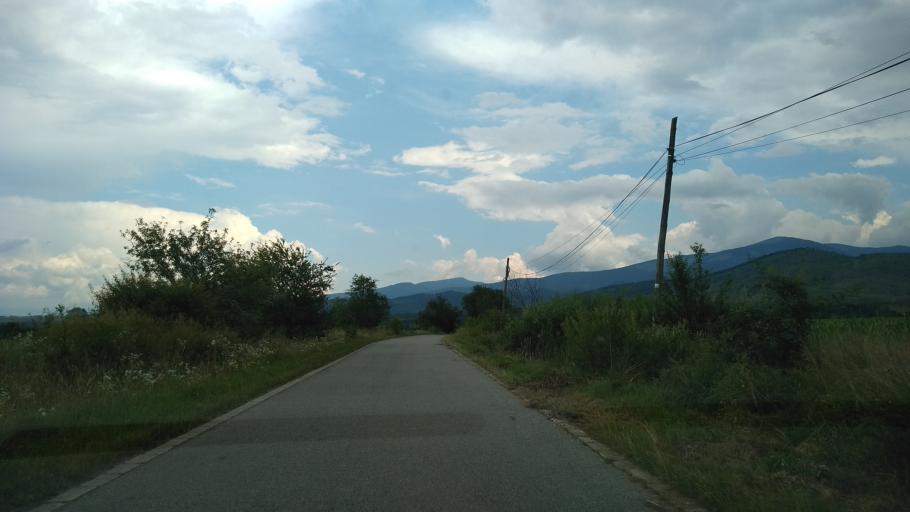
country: RO
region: Hunedoara
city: Salasu de Sus
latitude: 45.5020
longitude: 22.9656
